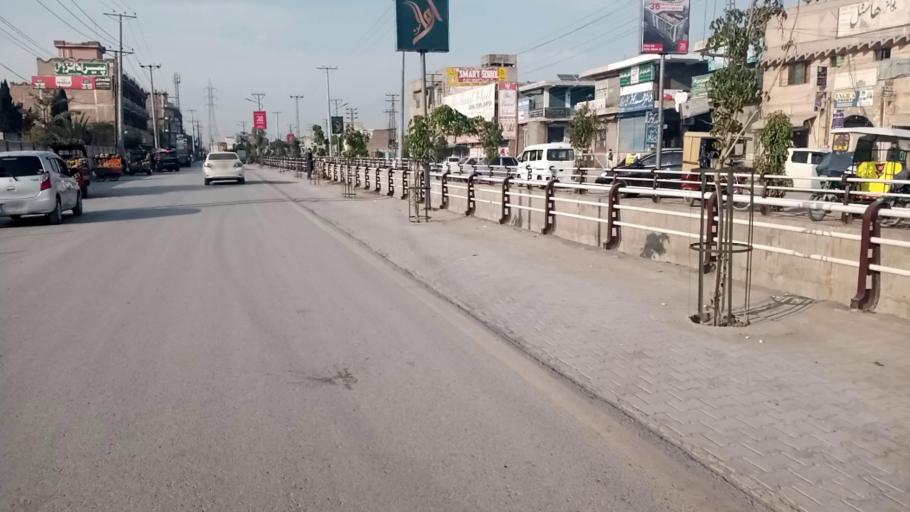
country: PK
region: Khyber Pakhtunkhwa
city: Peshawar
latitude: 33.9995
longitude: 71.4689
